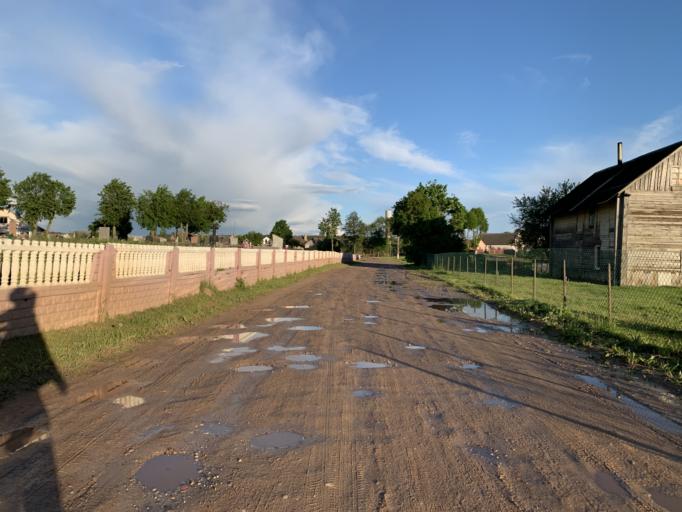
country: BY
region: Minsk
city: Nyasvizh
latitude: 53.2086
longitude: 26.6946
